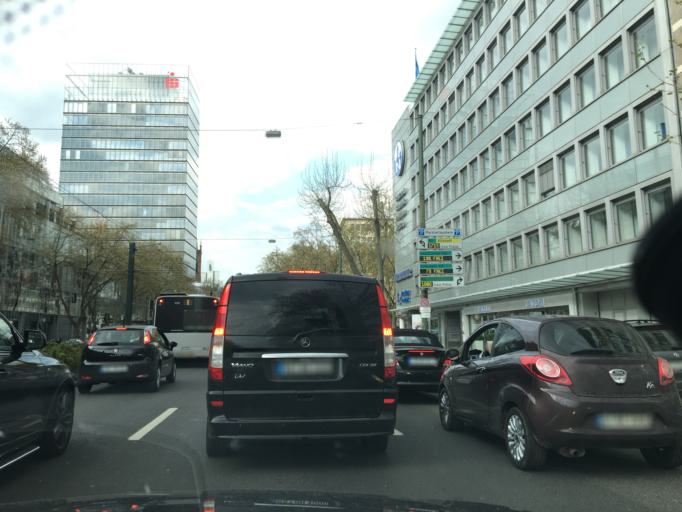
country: DE
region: North Rhine-Westphalia
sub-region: Regierungsbezirk Dusseldorf
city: Dusseldorf
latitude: 51.2209
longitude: 6.7824
